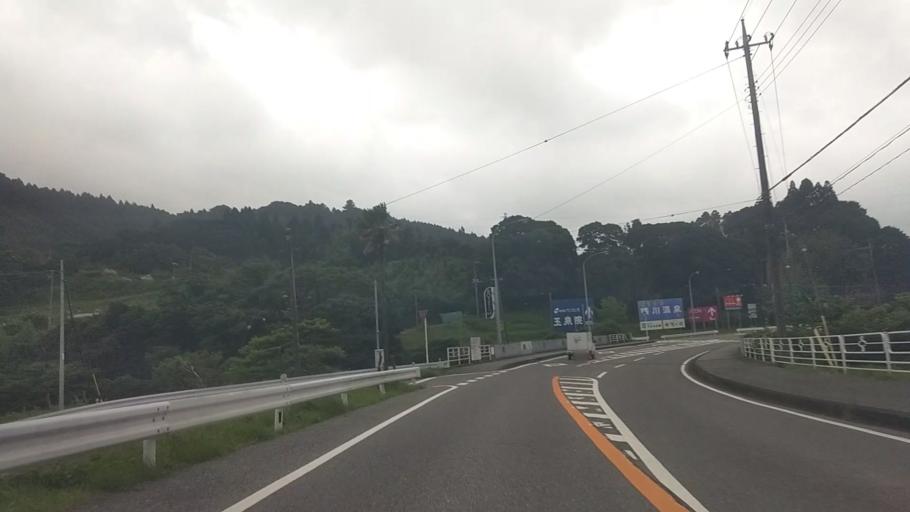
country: JP
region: Chiba
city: Kawaguchi
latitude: 35.1441
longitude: 140.0696
